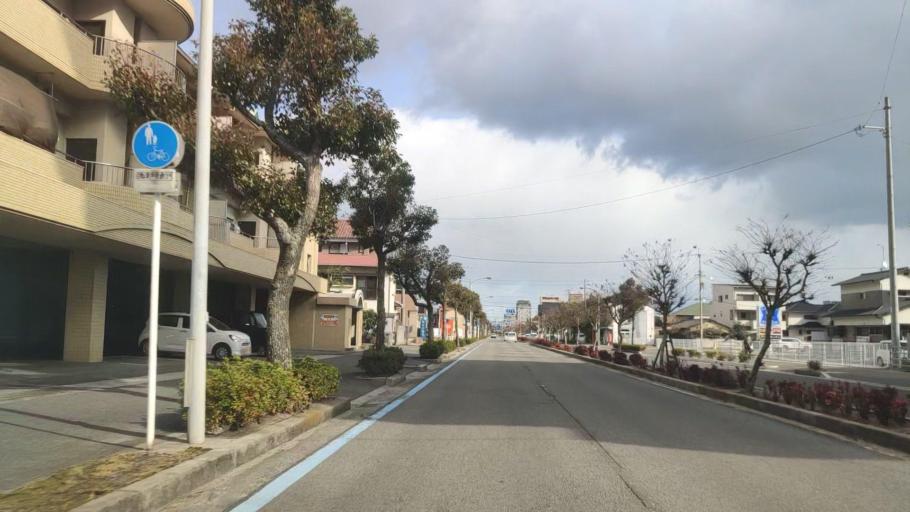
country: JP
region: Ehime
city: Hojo
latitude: 34.0613
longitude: 132.9850
